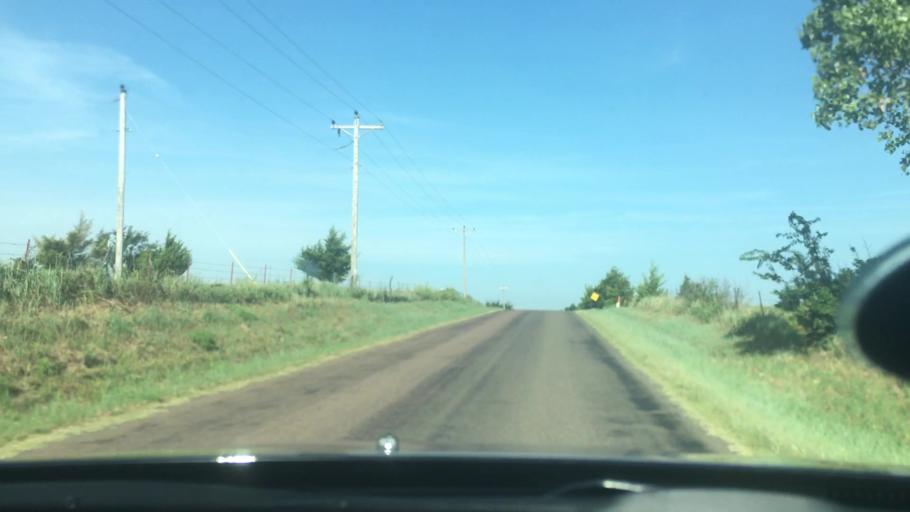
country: US
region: Oklahoma
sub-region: Garvin County
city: Maysville
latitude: 34.6521
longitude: -97.3838
